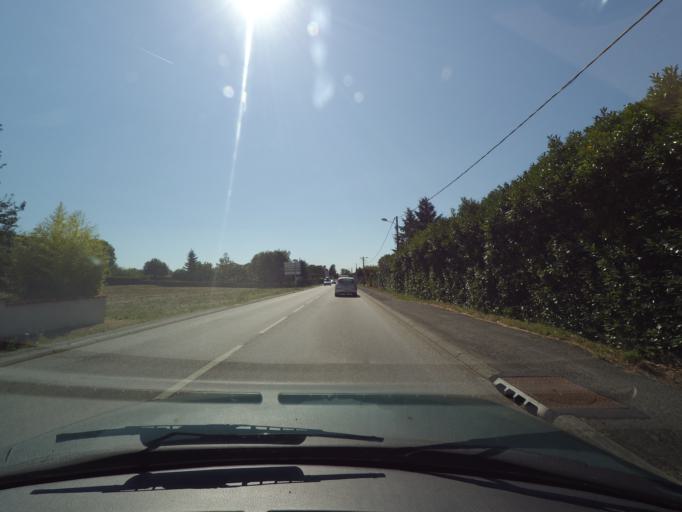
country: FR
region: Limousin
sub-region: Departement de la Haute-Vienne
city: Bellac
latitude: 46.0714
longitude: 1.1021
